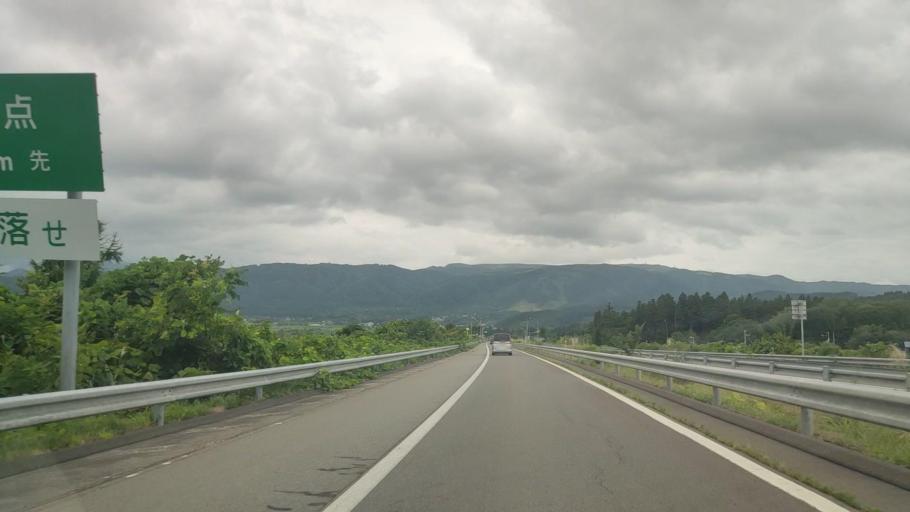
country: JP
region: Hokkaido
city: Nanae
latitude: 41.9208
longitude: 140.6779
